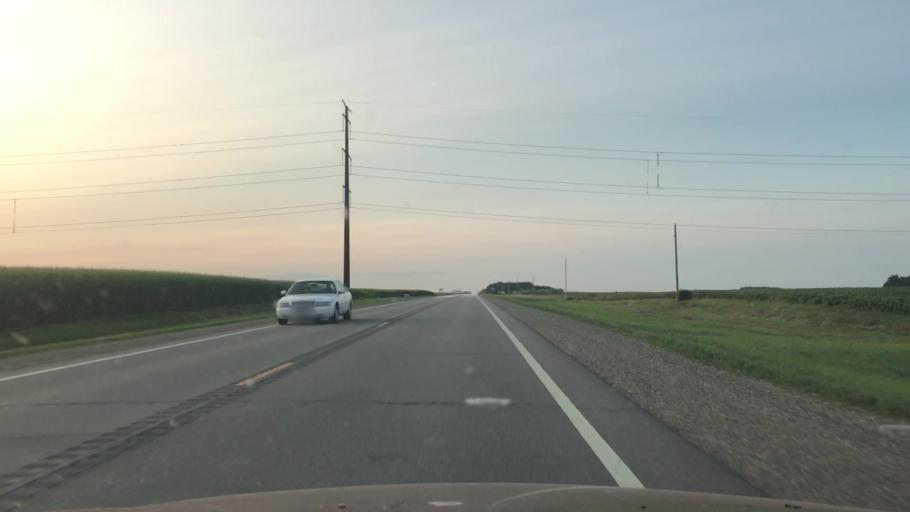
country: US
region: Minnesota
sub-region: Redwood County
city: Redwood Falls
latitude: 44.4327
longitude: -95.1176
